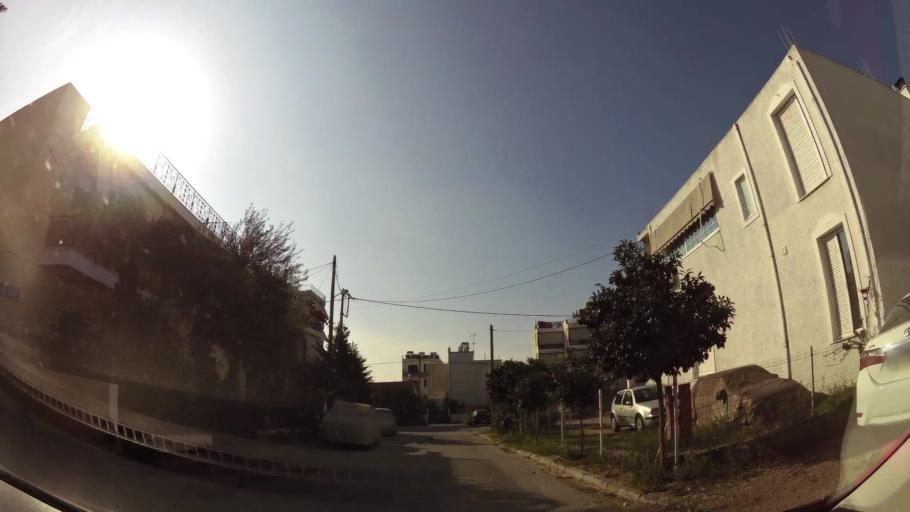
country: GR
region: Attica
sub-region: Nomarchia Anatolikis Attikis
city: Acharnes
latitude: 38.0630
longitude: 23.7402
